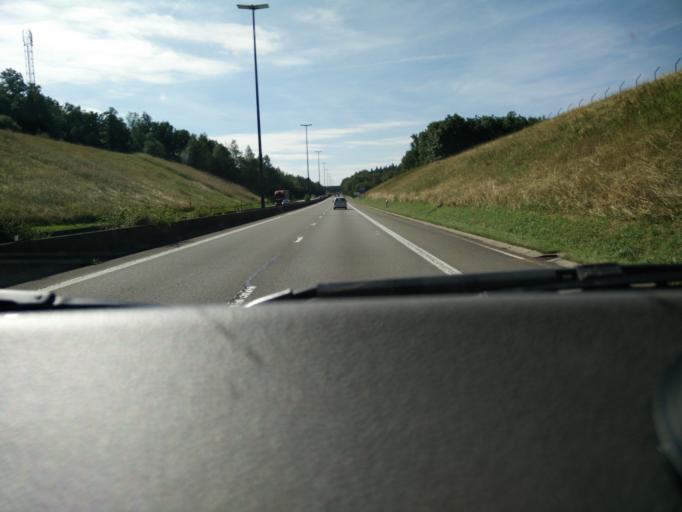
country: BE
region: Wallonia
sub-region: Province du Luxembourg
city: Libin
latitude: 49.9584
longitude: 5.2378
